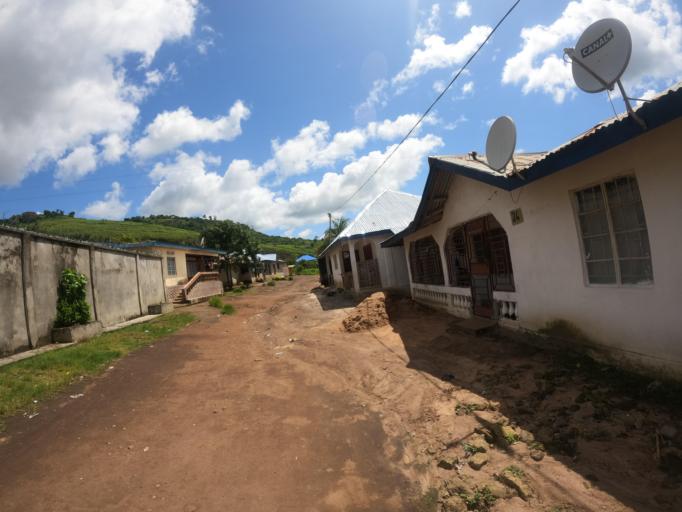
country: SL
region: Northern Province
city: Makeni
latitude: 8.8863
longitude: -12.0663
